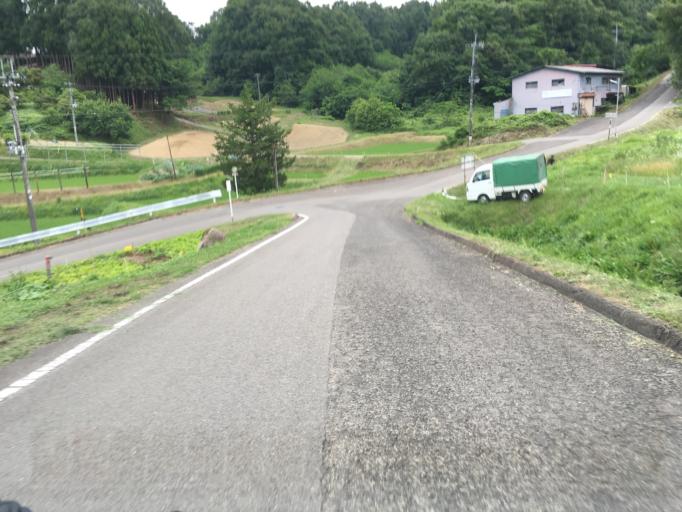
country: JP
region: Fukushima
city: Nihommatsu
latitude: 37.6260
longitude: 140.5280
